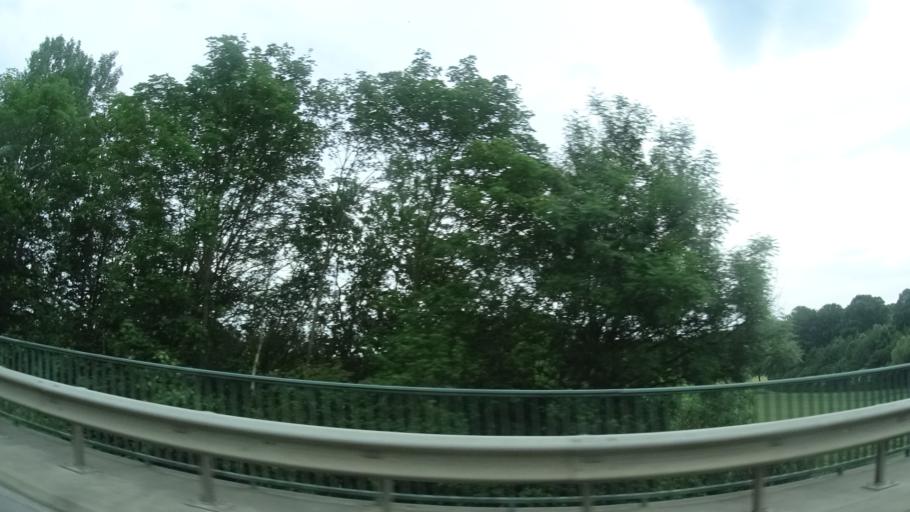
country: DE
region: North Rhine-Westphalia
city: Brakel
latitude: 51.7019
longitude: 9.1709
